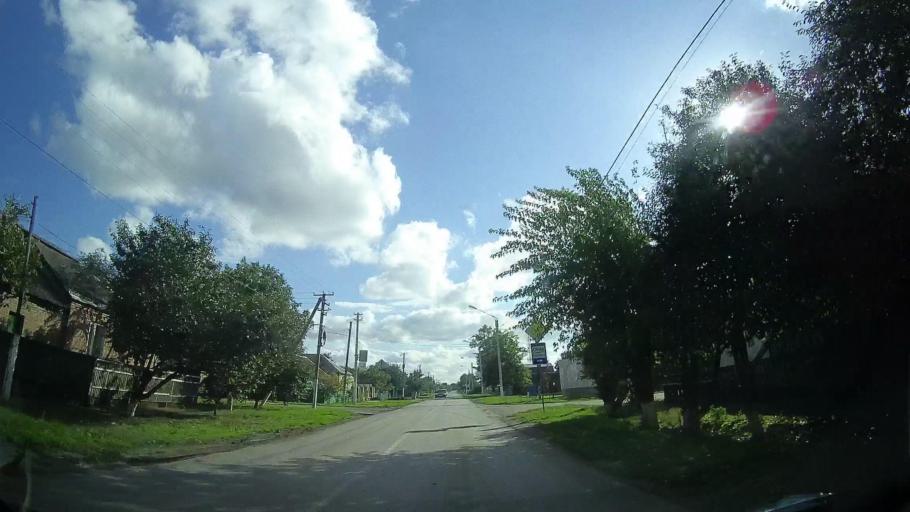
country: RU
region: Rostov
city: Tselina
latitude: 46.5370
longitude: 41.0341
